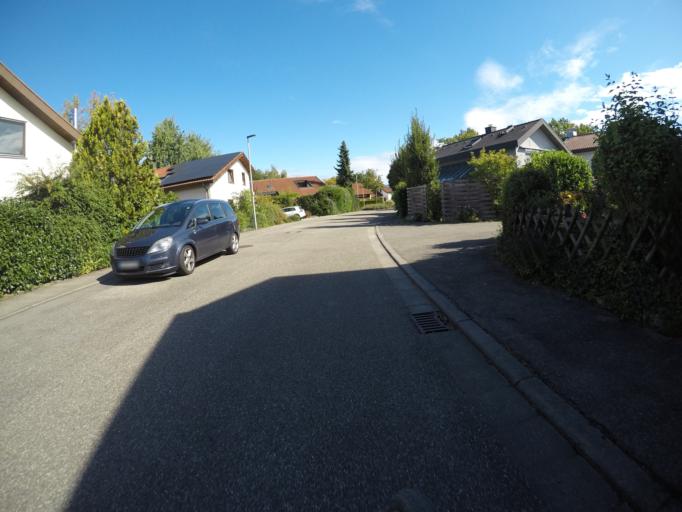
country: DE
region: Baden-Wuerttemberg
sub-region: Regierungsbezirk Stuttgart
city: Pleidelsheim
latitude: 48.9573
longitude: 9.1961
